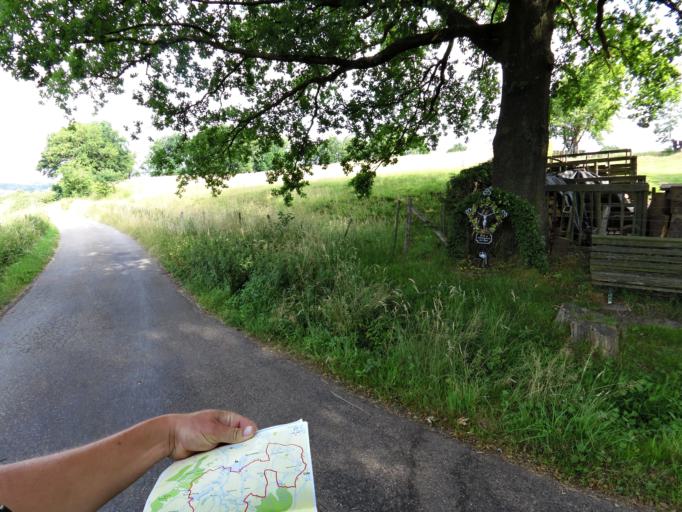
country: BE
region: Wallonia
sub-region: Province de Liege
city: Plombieres
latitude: 50.7827
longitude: 5.9308
